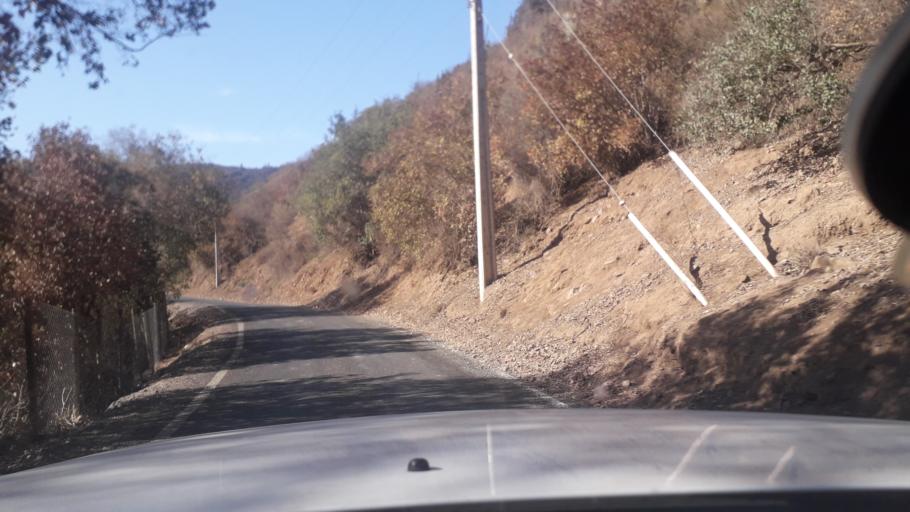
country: CL
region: Valparaiso
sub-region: Provincia de Marga Marga
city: Limache
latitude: -33.0703
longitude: -71.0980
